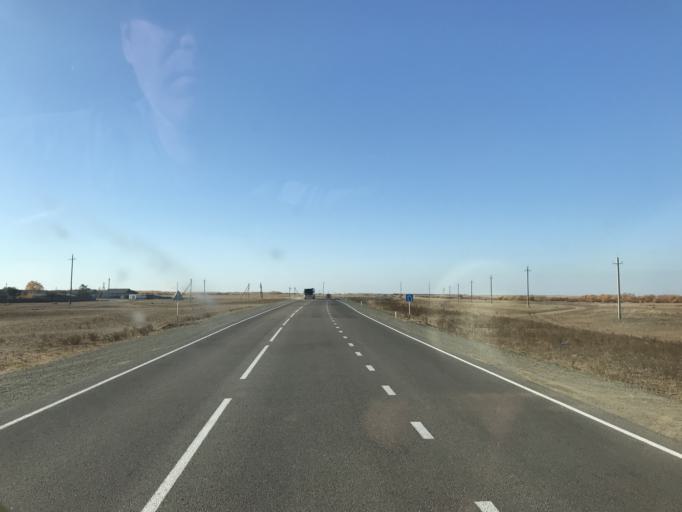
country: KZ
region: Pavlodar
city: Koktobe
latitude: 51.5058
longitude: 77.6938
